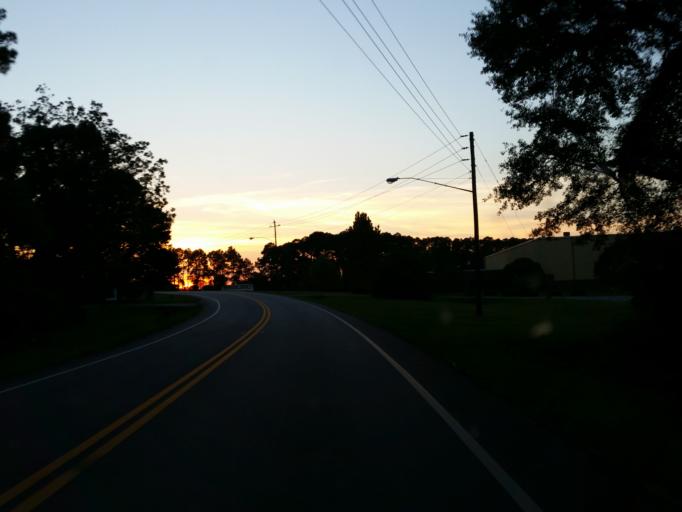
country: US
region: Georgia
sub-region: Tift County
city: Unionville
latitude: 31.4164
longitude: -83.4887
